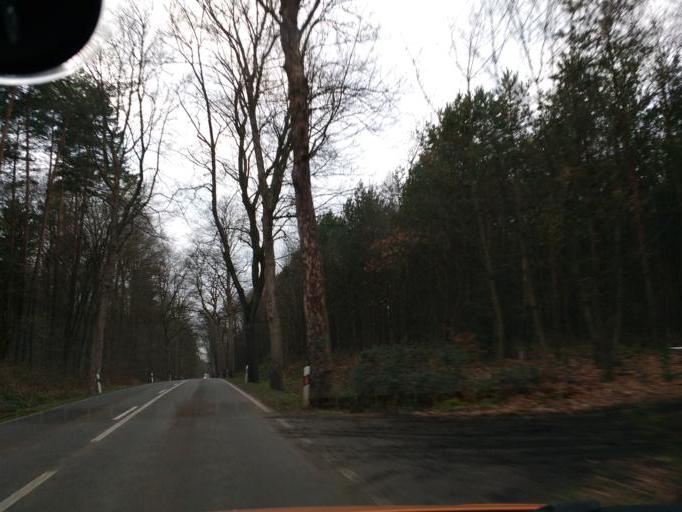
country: DE
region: Brandenburg
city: Strausberg
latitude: 52.6558
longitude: 13.8870
